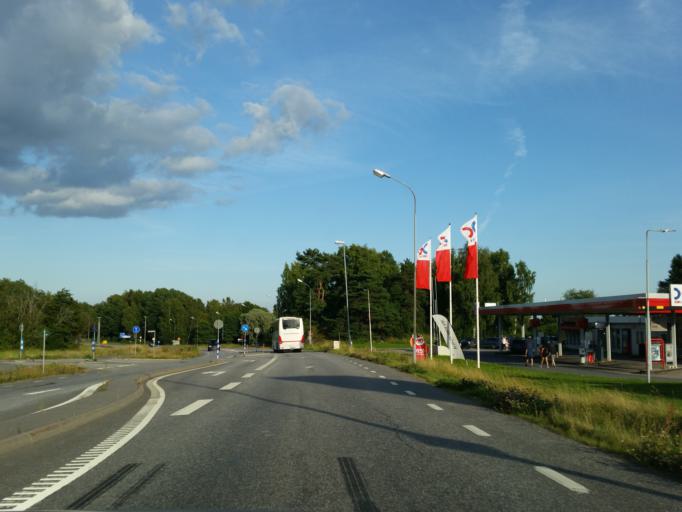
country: SE
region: Stockholm
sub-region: Sodertalje Kommun
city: Pershagen
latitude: 59.0876
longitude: 17.5782
